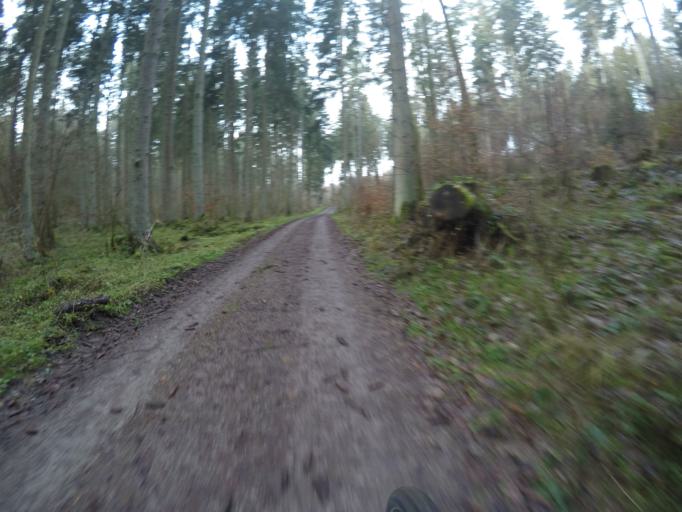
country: DE
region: Baden-Wuerttemberg
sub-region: Regierungsbezirk Stuttgart
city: Deckenpfronn
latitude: 48.6641
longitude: 8.8249
